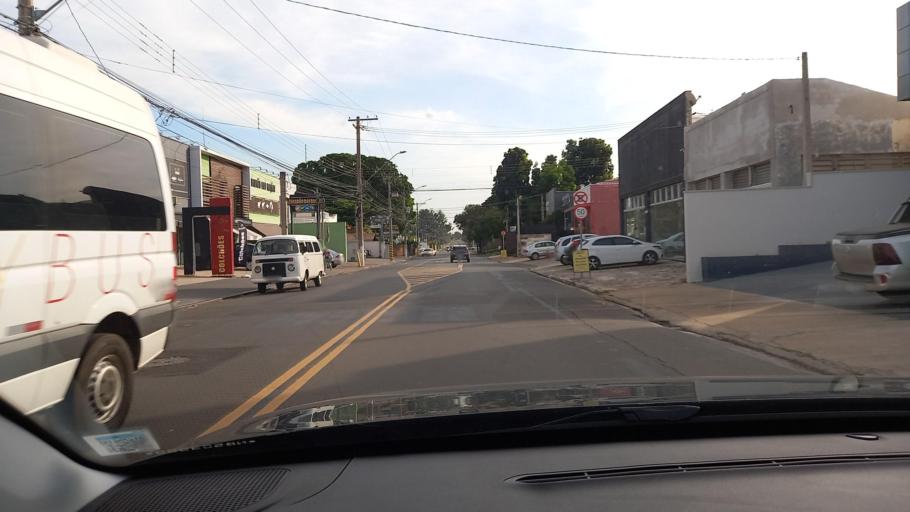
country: BR
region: Sao Paulo
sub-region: Mogi-Mirim
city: Mogi Mirim
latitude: -22.4436
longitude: -46.9719
